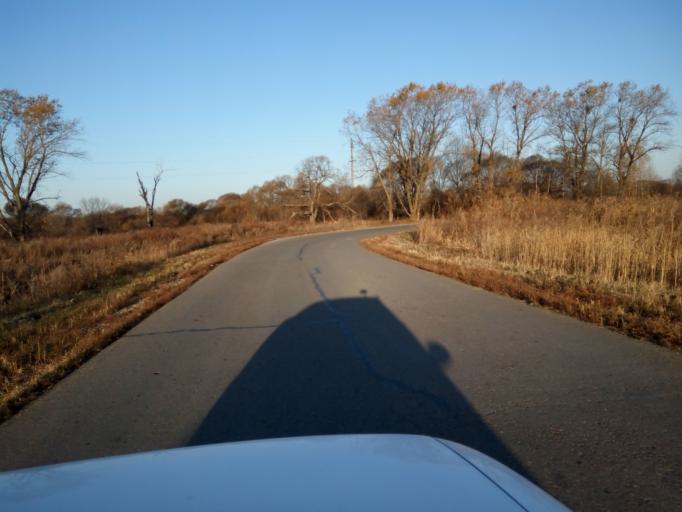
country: RU
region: Primorskiy
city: Lazo
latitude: 45.8586
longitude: 133.6403
